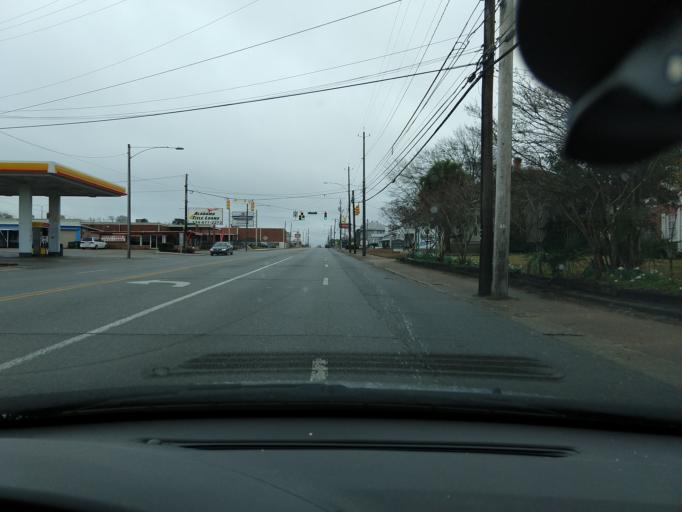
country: US
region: Alabama
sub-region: Houston County
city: Dothan
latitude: 31.2259
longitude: -85.4031
